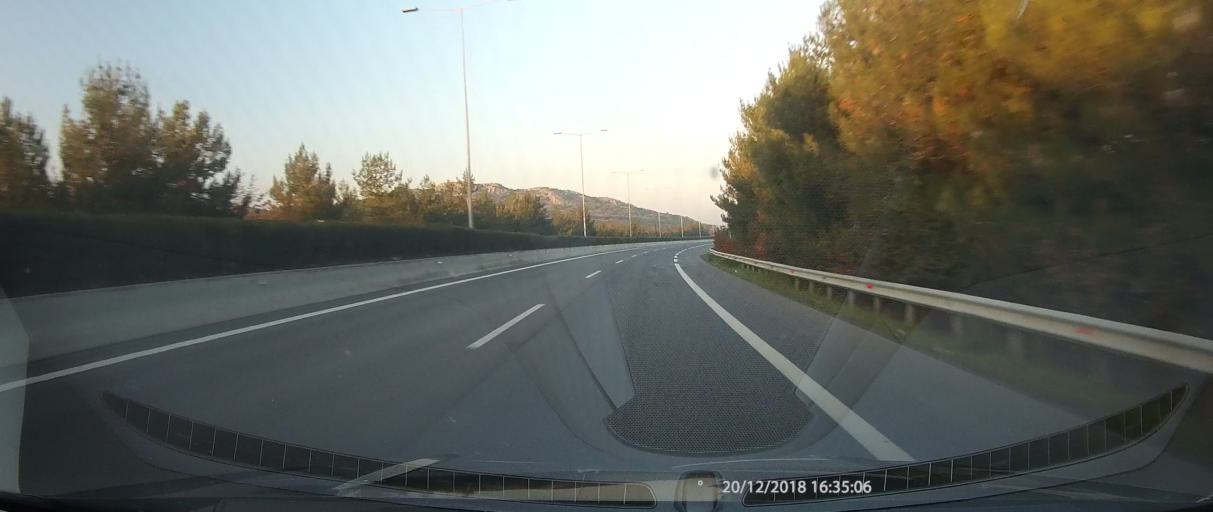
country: GR
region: Thessaly
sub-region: Nomos Magnisias
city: Nea Anchialos
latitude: 39.2966
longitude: 22.7447
